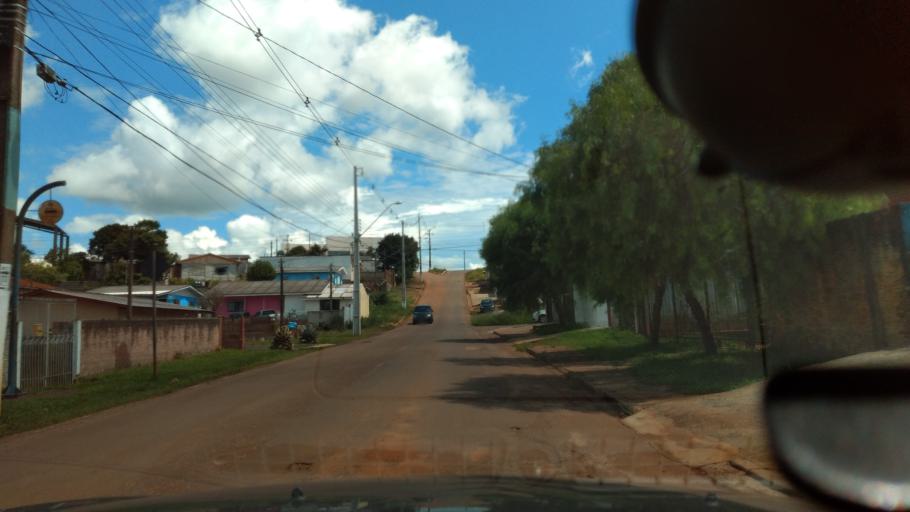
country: BR
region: Parana
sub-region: Guarapuava
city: Guarapuava
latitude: -25.3945
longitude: -51.4990
